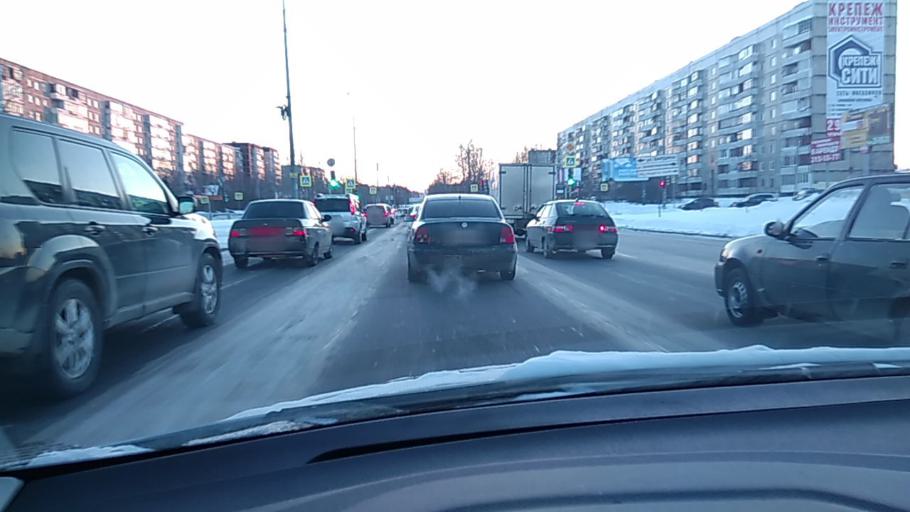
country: RU
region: Sverdlovsk
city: Sovkhoznyy
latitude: 56.8107
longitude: 60.5470
